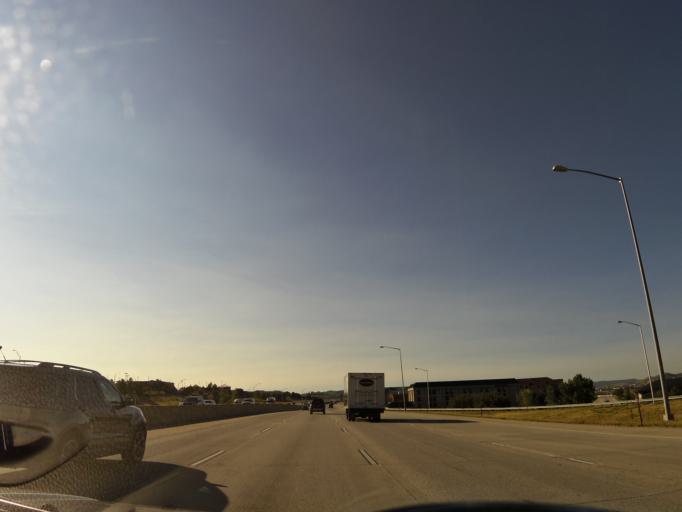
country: US
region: Colorado
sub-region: Douglas County
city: Castle Rock
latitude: 39.4122
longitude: -104.8678
